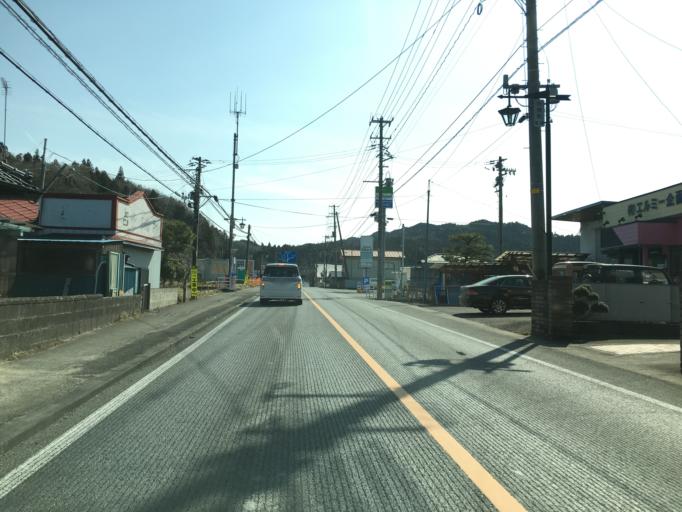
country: JP
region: Ibaraki
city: Daigo
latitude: 36.8677
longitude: 140.4247
